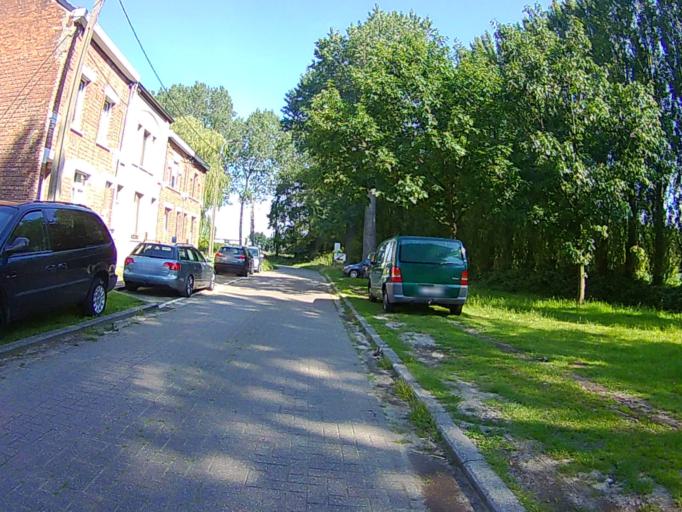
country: BE
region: Flanders
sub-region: Provincie Antwerpen
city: Zwijndrecht
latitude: 51.2040
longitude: 4.3321
